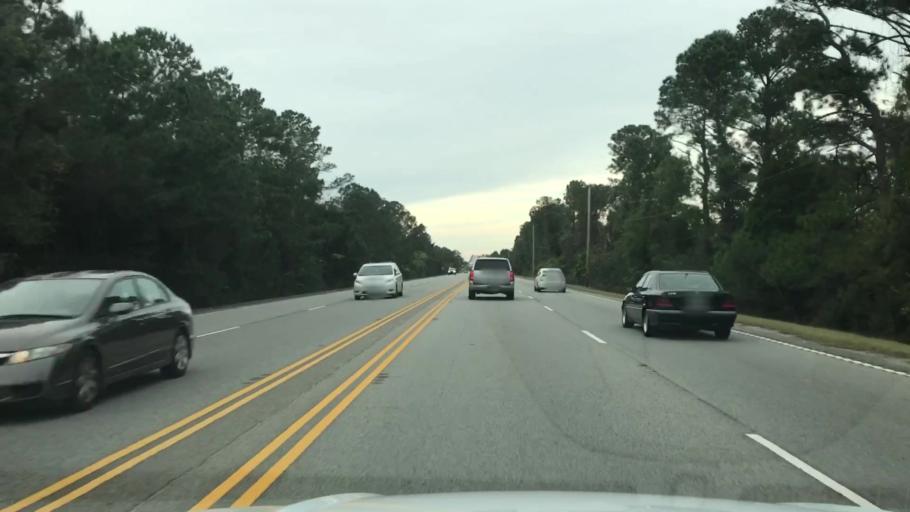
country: US
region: South Carolina
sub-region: Georgetown County
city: Georgetown
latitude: 33.3647
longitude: -79.2419
